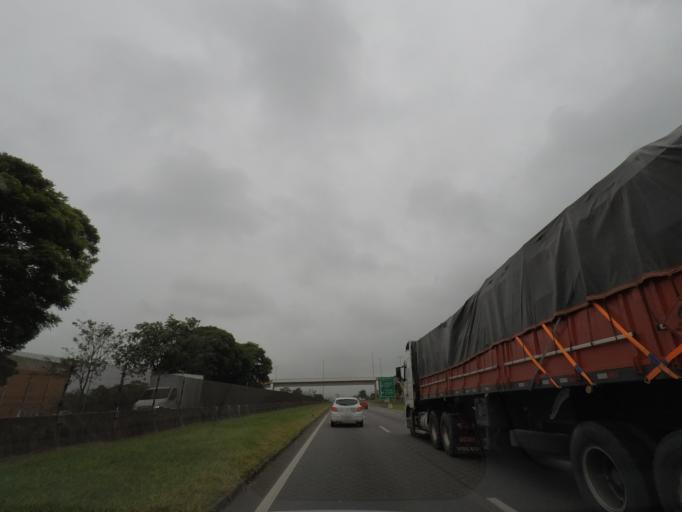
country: BR
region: Sao Paulo
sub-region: Cacapava
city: Cacapava
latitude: -23.1178
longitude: -45.7175
